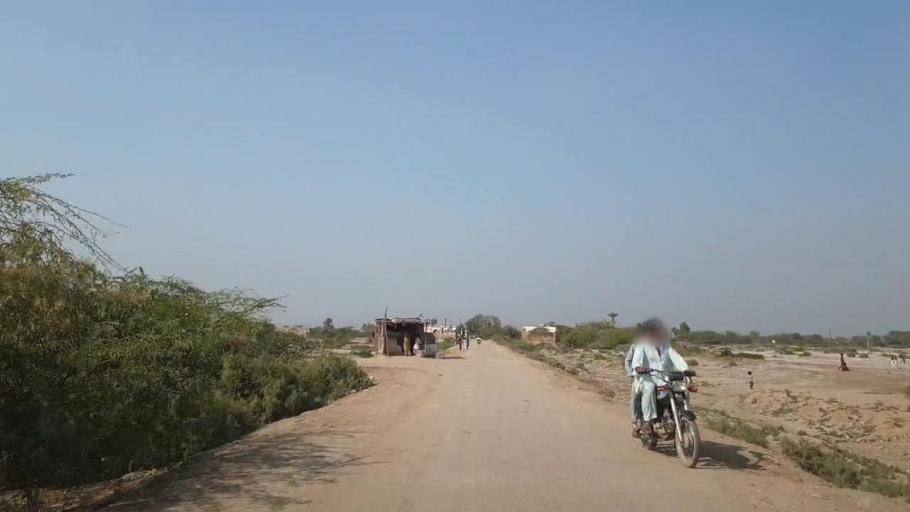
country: PK
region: Sindh
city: Mirpur Khas
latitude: 25.5011
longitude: 68.8849
